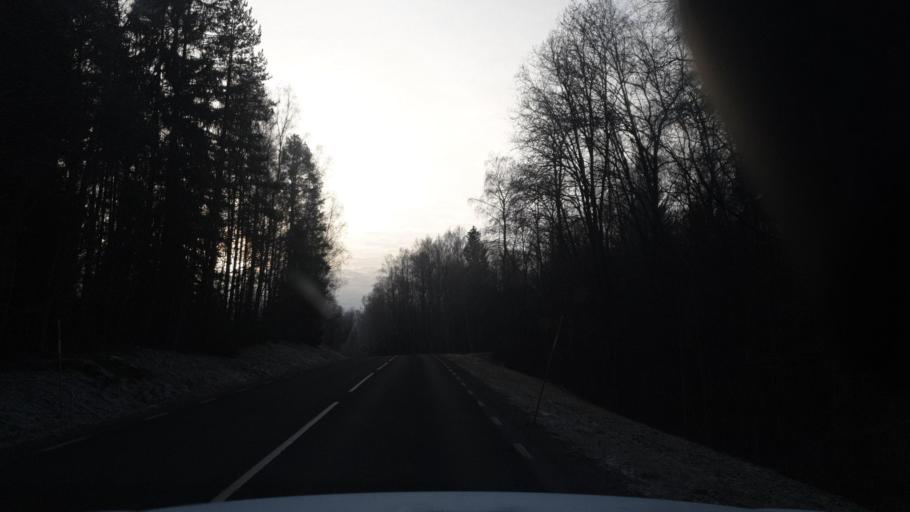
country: SE
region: Vaermland
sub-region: Eda Kommun
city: Amotfors
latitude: 59.7105
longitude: 12.4364
